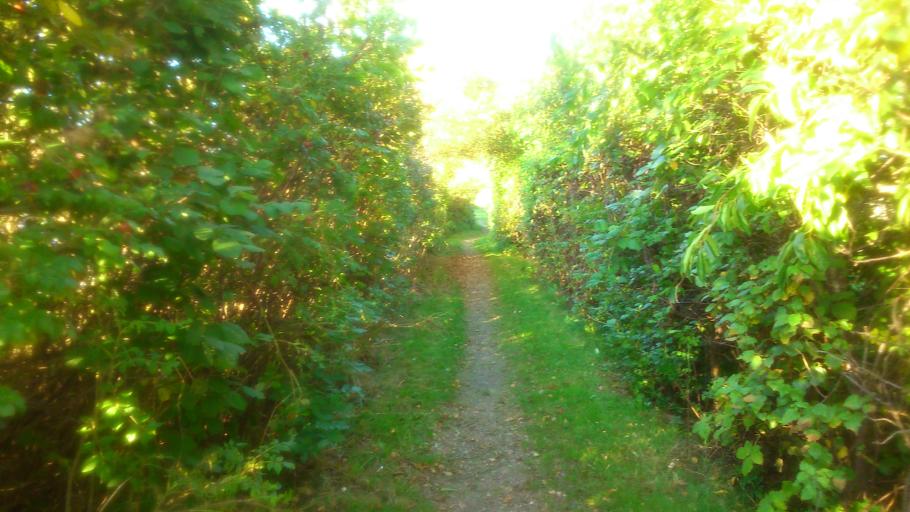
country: DK
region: Central Jutland
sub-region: Ringkobing-Skjern Kommune
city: Hvide Sande
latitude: 55.8486
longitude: 8.2826
